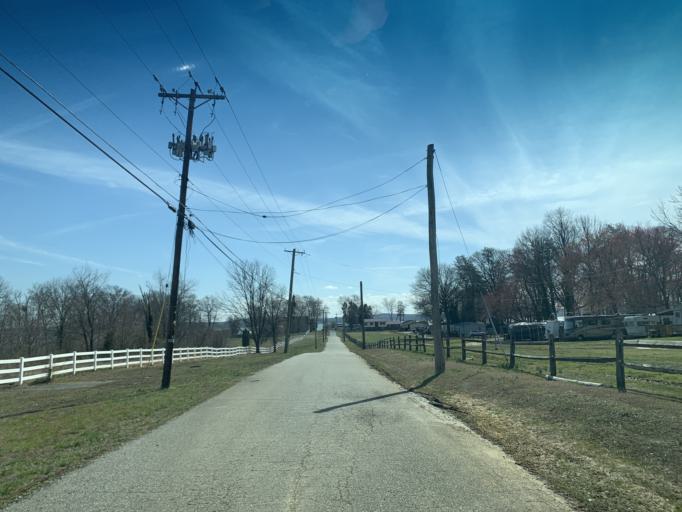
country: US
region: Maryland
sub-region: Cecil County
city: Charlestown
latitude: 39.5536
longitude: -76.0080
